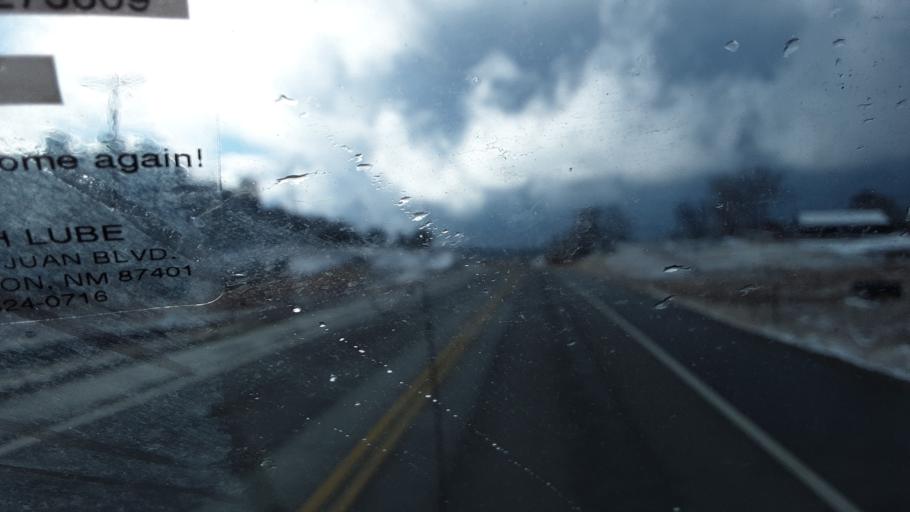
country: US
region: Colorado
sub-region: La Plata County
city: Bayfield
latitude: 37.2213
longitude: -107.6274
